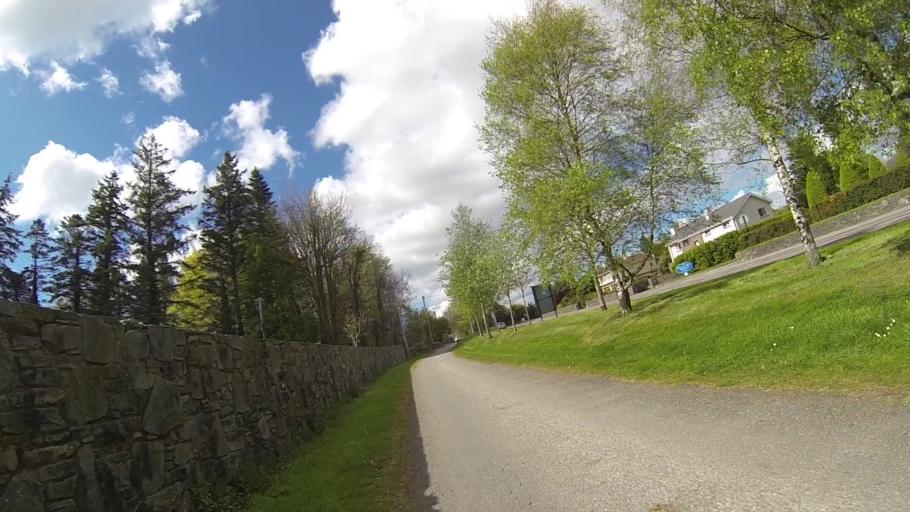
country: IE
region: Munster
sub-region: Ciarrai
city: Cill Airne
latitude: 52.0461
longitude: -9.5056
